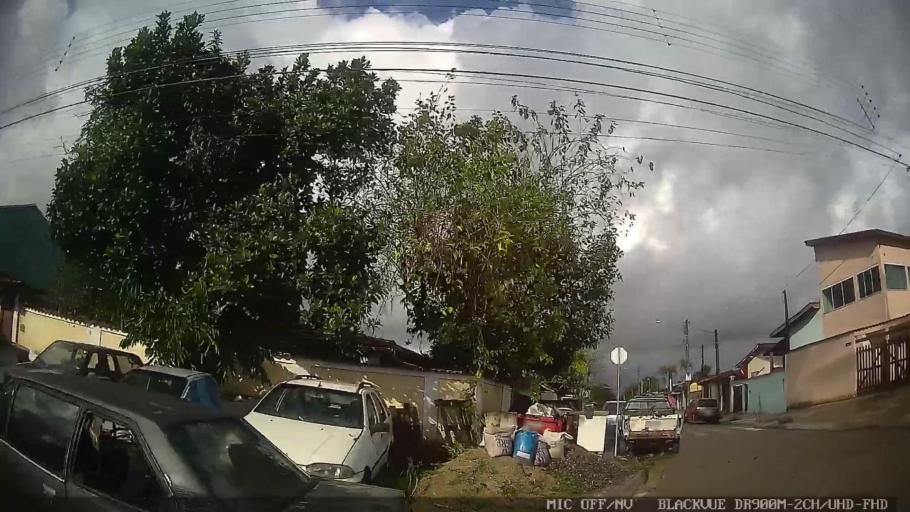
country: BR
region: Sao Paulo
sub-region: Itanhaem
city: Itanhaem
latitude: -24.2132
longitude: -46.8807
